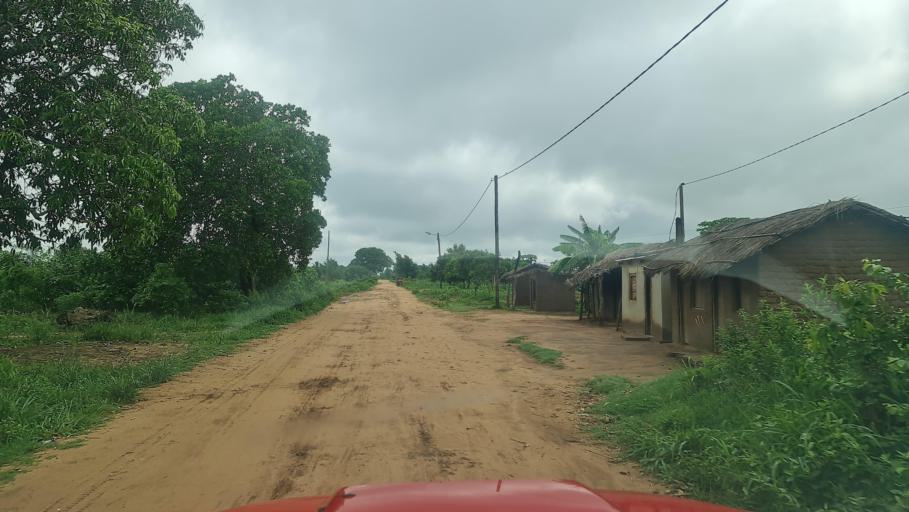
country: MW
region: Southern Region
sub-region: Nsanje District
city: Nsanje
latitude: -17.1902
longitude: 35.7099
